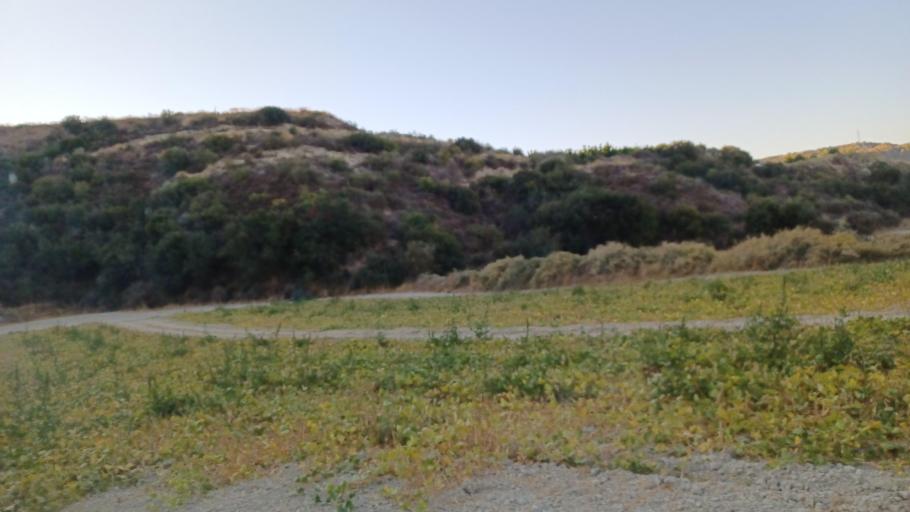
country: CY
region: Pafos
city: Polis
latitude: 34.9863
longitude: 32.4659
